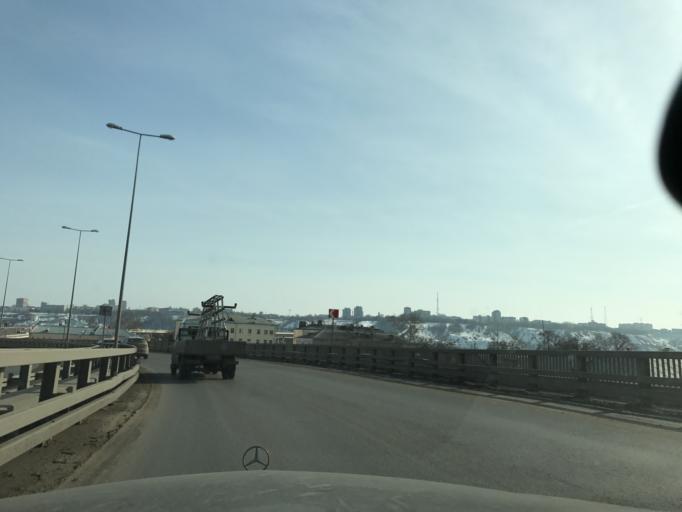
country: RU
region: Nizjnij Novgorod
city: Nizhniy Novgorod
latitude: 56.3219
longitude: 43.9497
